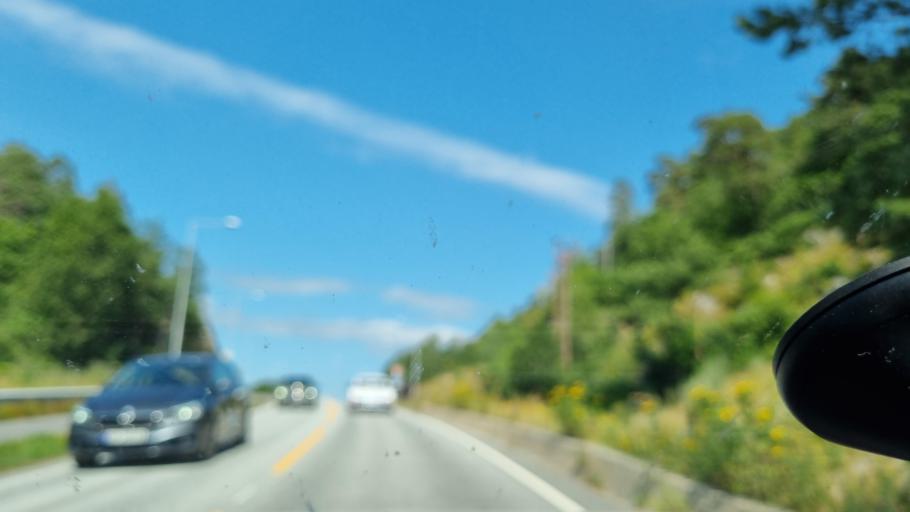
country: NO
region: Aust-Agder
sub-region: Arendal
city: Arendal
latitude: 58.4580
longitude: 8.8193
